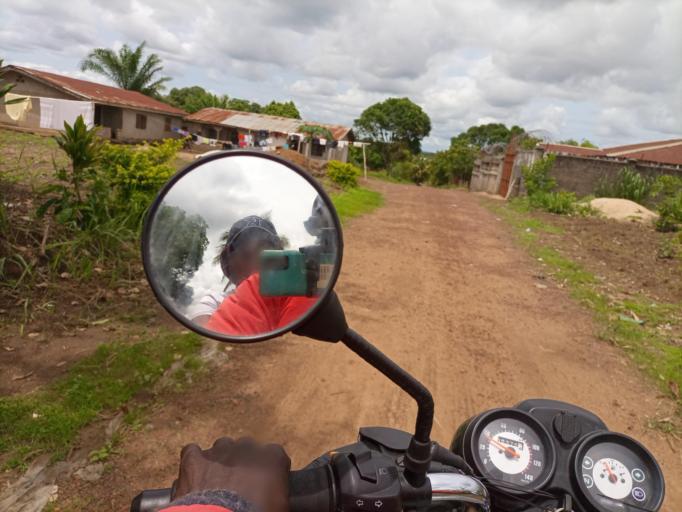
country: SL
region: Southern Province
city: Baoma
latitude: 7.9704
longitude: -11.7142
